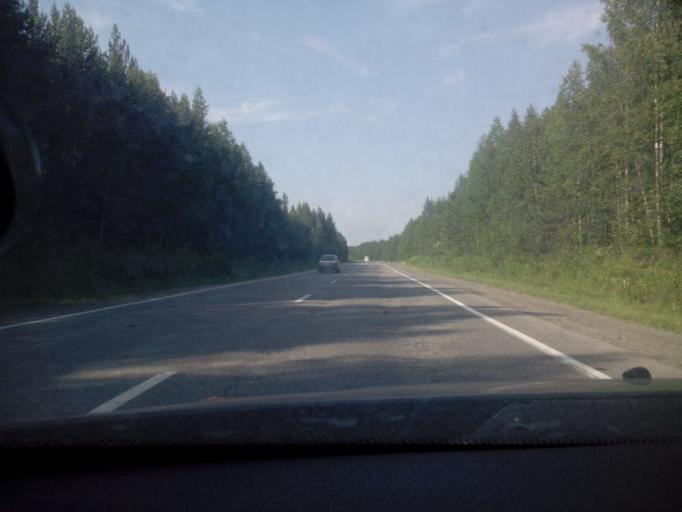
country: RU
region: Sverdlovsk
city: Verkh-Neyvinskiy
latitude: 57.2612
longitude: 60.2897
